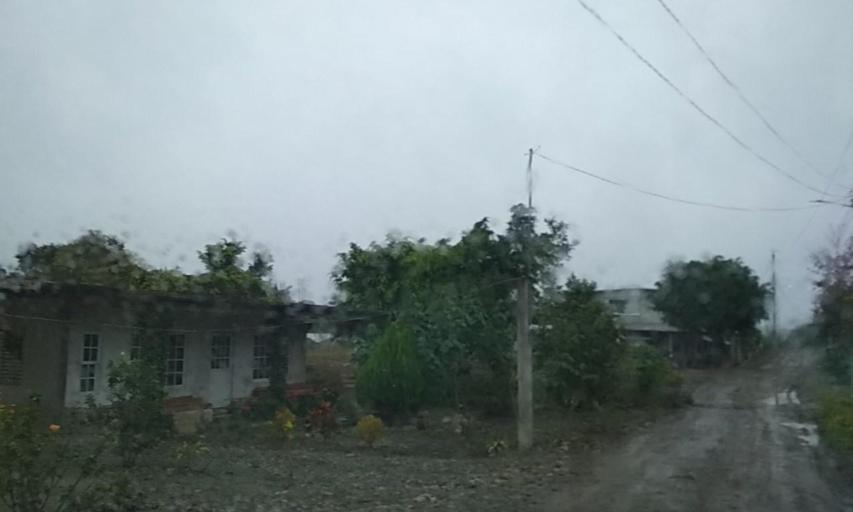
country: MX
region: Puebla
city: Espinal
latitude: 20.3297
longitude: -97.3940
